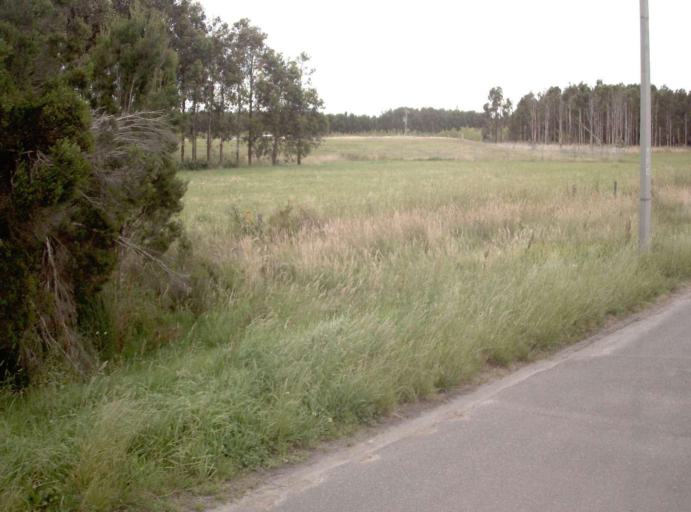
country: AU
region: Victoria
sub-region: Cardinia
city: Koo-Wee-Rup
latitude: -38.2725
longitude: 145.5479
